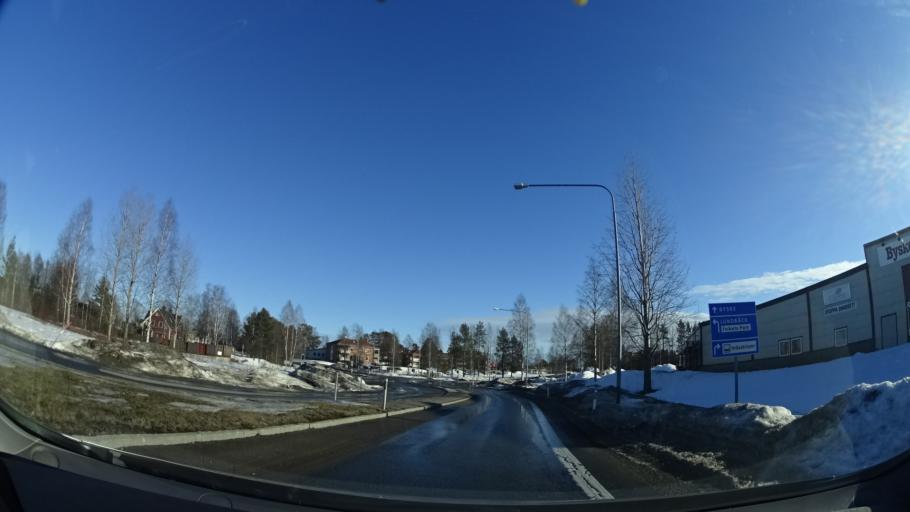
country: SE
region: Vaesterbotten
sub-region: Skelleftea Kommun
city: Byske
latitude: 64.9524
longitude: 21.1916
